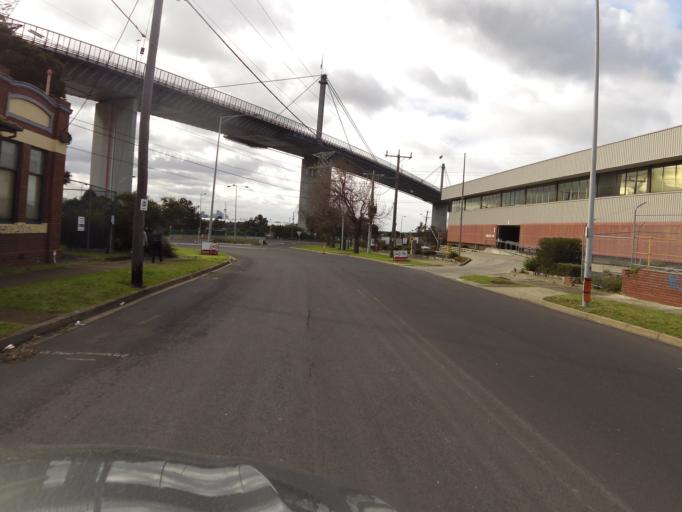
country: AU
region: Victoria
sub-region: Hobsons Bay
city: Spotswood
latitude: -37.8287
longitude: 144.8942
